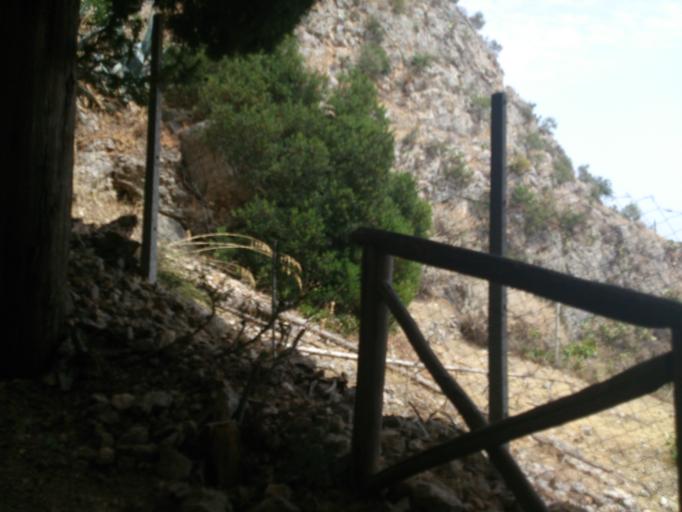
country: IT
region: Calabria
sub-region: Provincia di Reggio Calabria
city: Stilo
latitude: 38.4792
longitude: 16.4667
